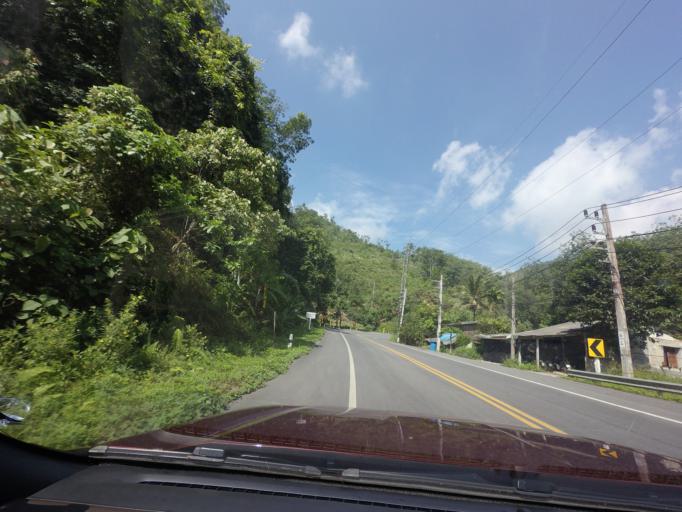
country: TH
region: Yala
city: Betong
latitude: 5.9192
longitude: 101.1606
